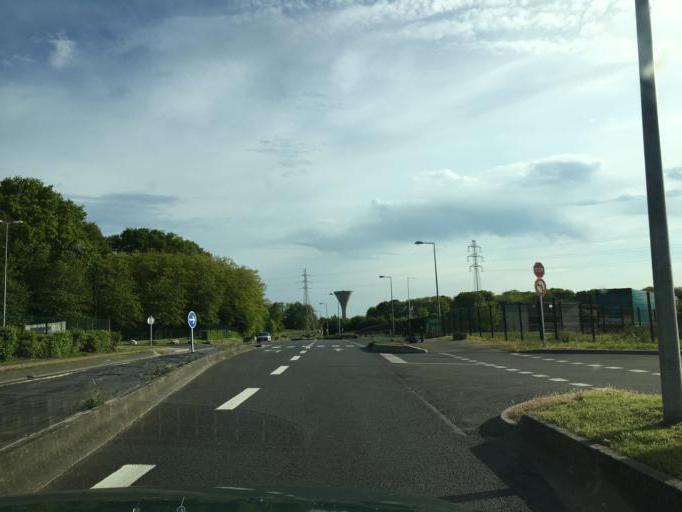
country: FR
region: Centre
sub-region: Departement du Loiret
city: Ormes
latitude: 47.9417
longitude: 1.8431
